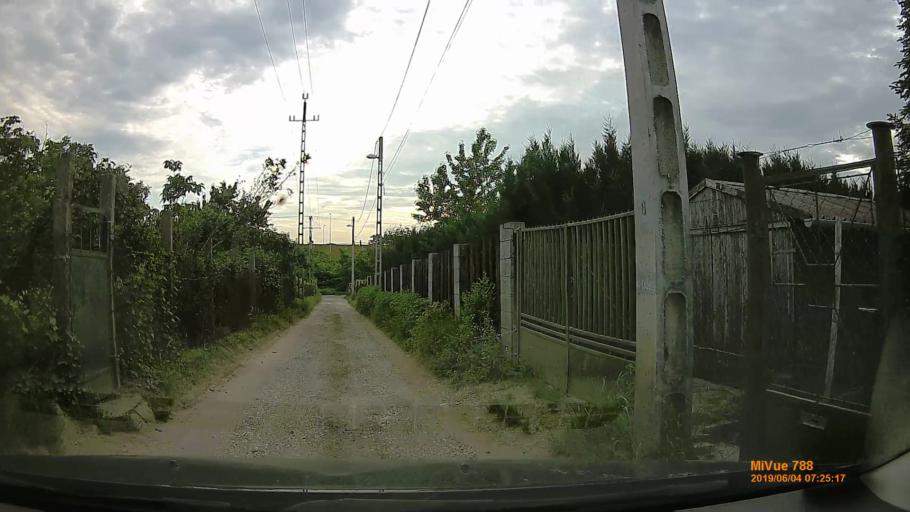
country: HU
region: Pest
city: Diosd
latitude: 47.4028
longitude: 18.9681
